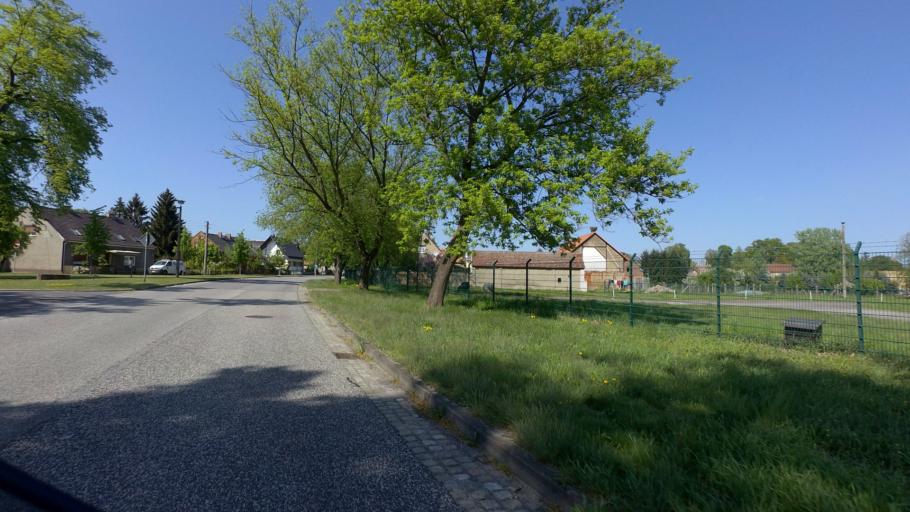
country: DE
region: Brandenburg
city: Neu Zauche
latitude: 52.0353
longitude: 14.0378
